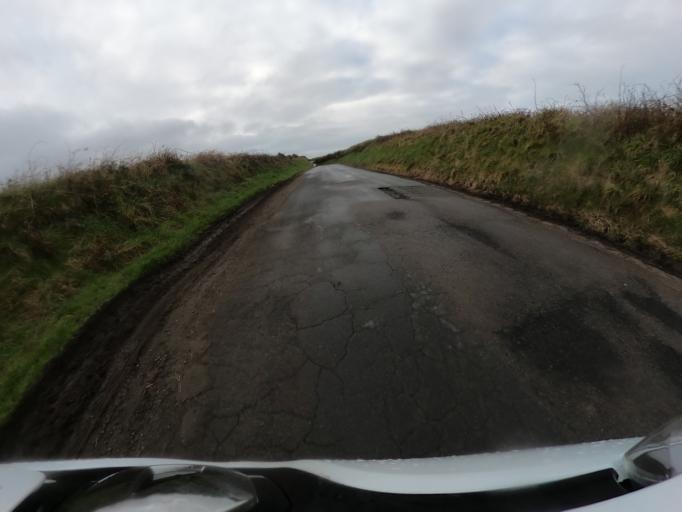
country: IM
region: Ramsey
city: Ramsey
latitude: 54.3633
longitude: -4.4661
